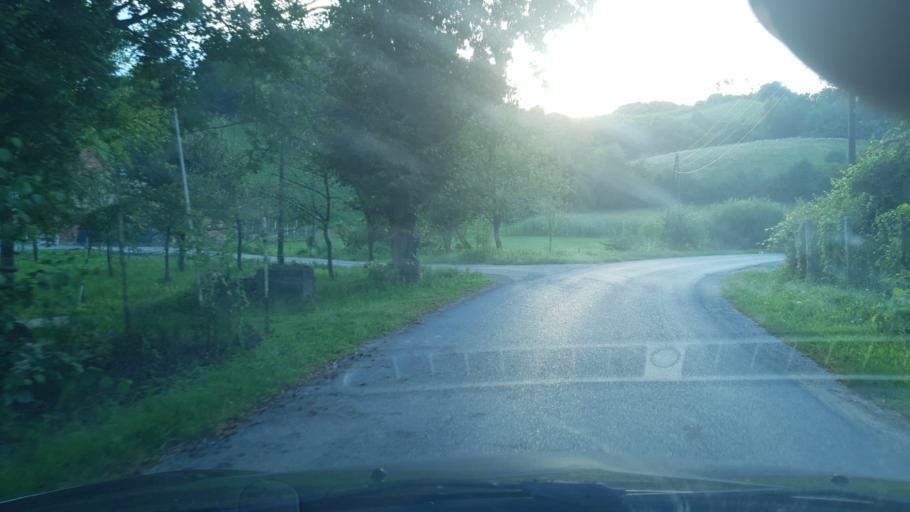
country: HR
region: Krapinsko-Zagorska
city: Zabok
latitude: 46.0507
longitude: 15.8882
